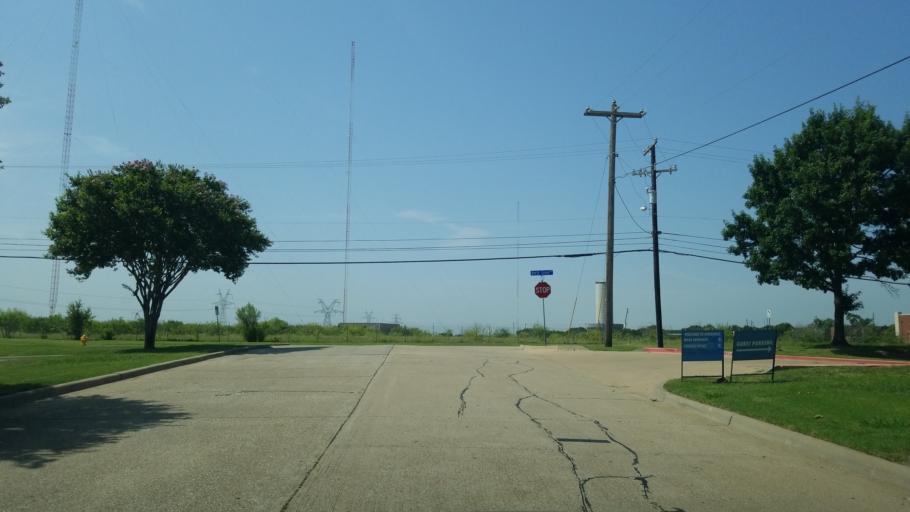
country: US
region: Texas
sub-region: Dallas County
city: Coppell
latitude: 32.9483
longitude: -96.9908
